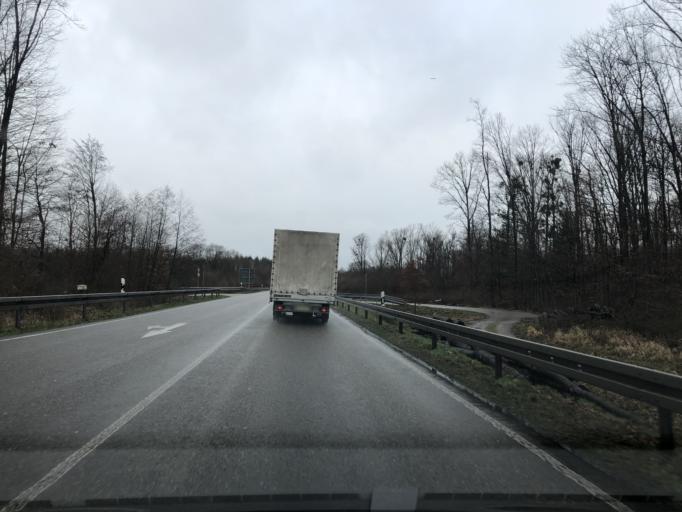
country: DE
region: Baden-Wuerttemberg
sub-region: Karlsruhe Region
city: Rastatt
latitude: 48.8267
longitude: 8.2063
